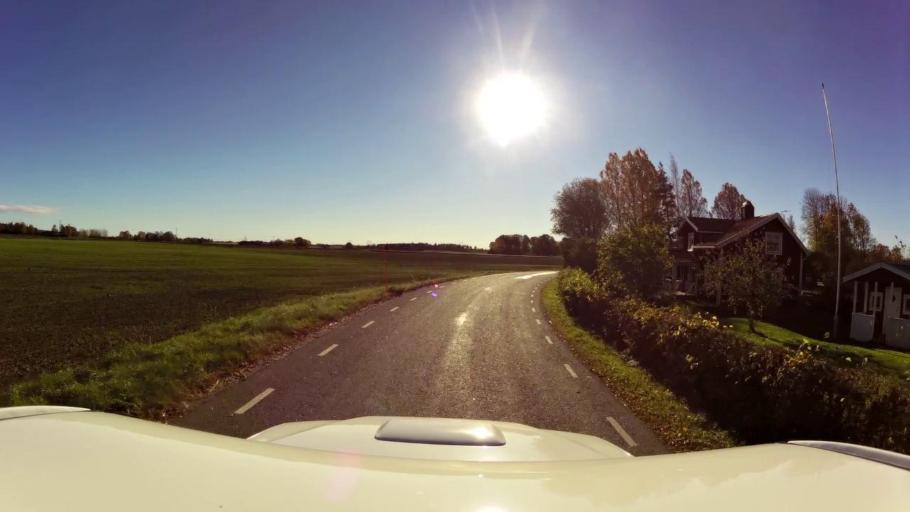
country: SE
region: OEstergoetland
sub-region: Linkopings Kommun
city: Ljungsbro
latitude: 58.4831
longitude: 15.4192
